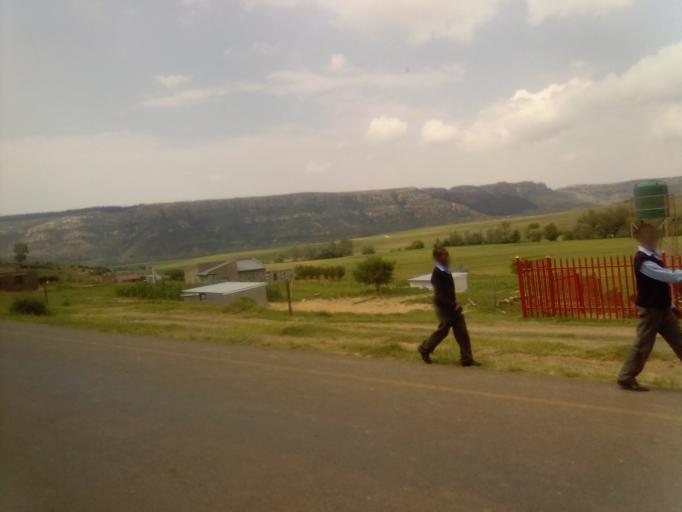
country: LS
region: Leribe
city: Leribe
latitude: -29.0201
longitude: 28.0009
